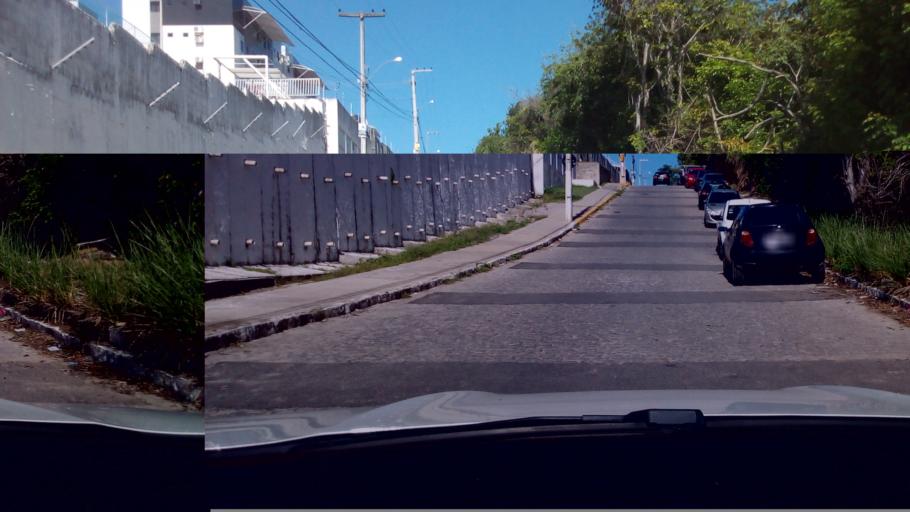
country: BR
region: Paraiba
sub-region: Joao Pessoa
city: Joao Pessoa
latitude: -7.1569
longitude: -34.8161
